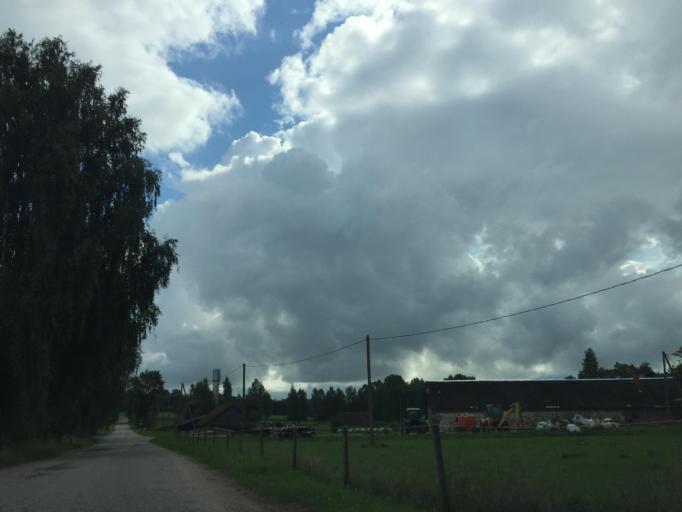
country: LV
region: Raunas
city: Rauna
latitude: 57.3350
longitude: 25.4882
